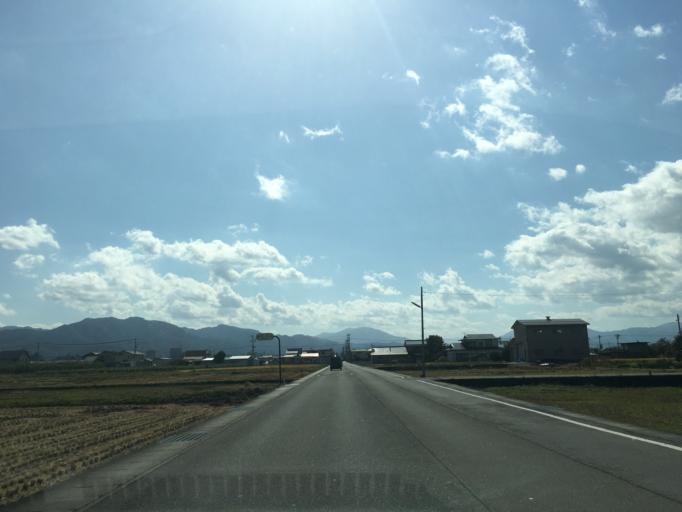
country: JP
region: Fukushima
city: Kitakata
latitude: 37.5132
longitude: 139.9197
